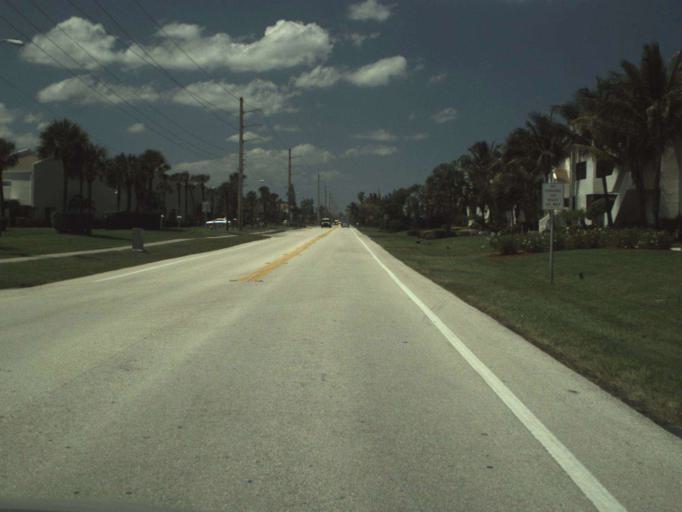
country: US
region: Florida
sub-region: Brevard County
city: Melbourne Beach
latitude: 28.0592
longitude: -80.5532
